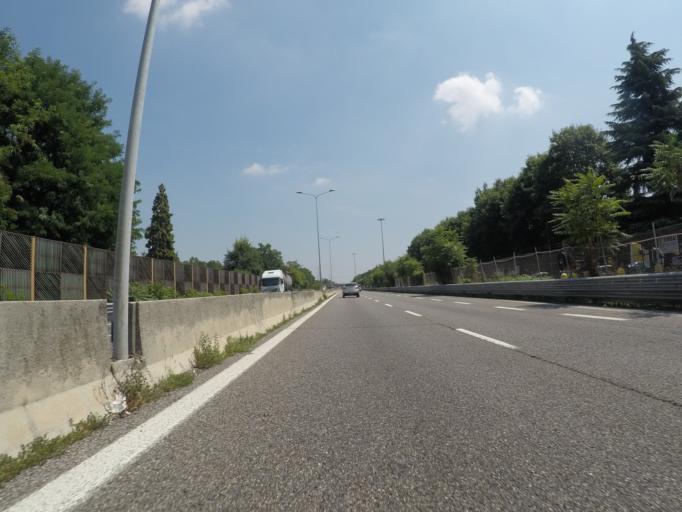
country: IT
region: Lombardy
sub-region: Provincia di Varese
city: Gallarate
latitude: 45.6402
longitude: 8.8125
